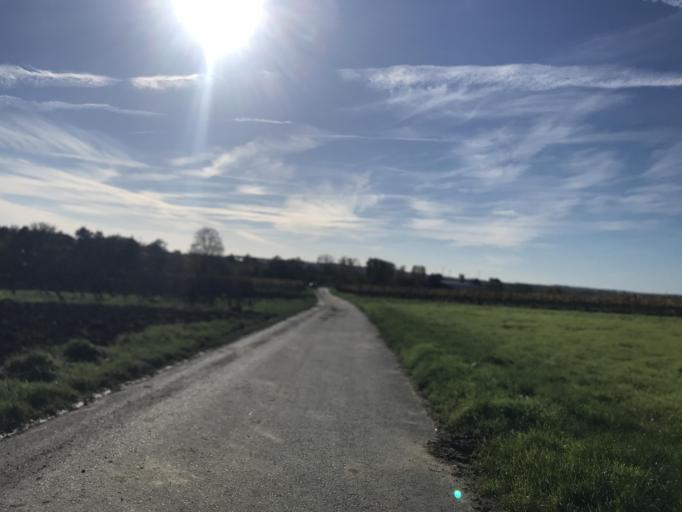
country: DE
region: Hesse
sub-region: Regierungsbezirk Darmstadt
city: Hochheim am Main
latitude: 50.0172
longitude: 8.3199
